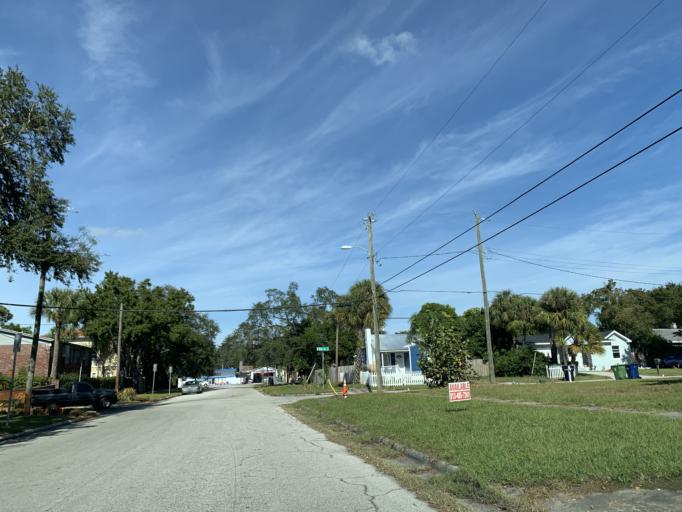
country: US
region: Florida
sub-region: Hillsborough County
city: Tampa
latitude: 27.8924
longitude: -82.5000
